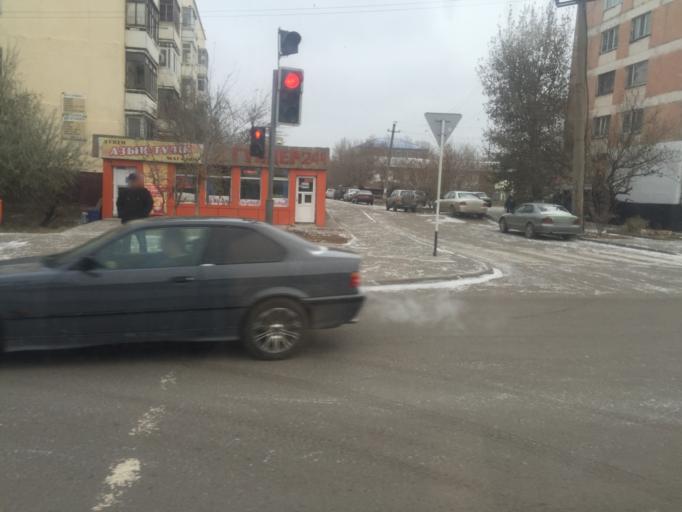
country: KZ
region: Astana Qalasy
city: Astana
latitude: 51.1986
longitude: 71.3928
